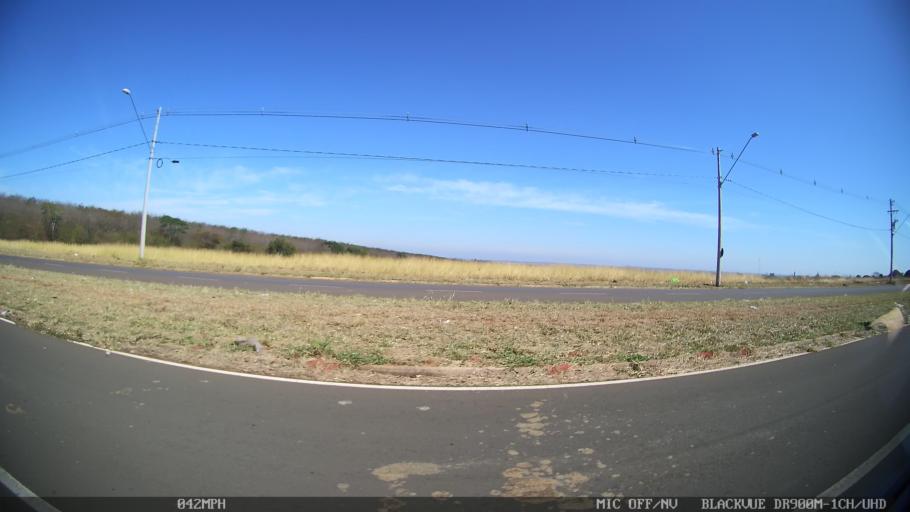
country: BR
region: Sao Paulo
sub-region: Sao Jose Do Rio Preto
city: Sao Jose do Rio Preto
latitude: -20.7332
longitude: -49.4364
